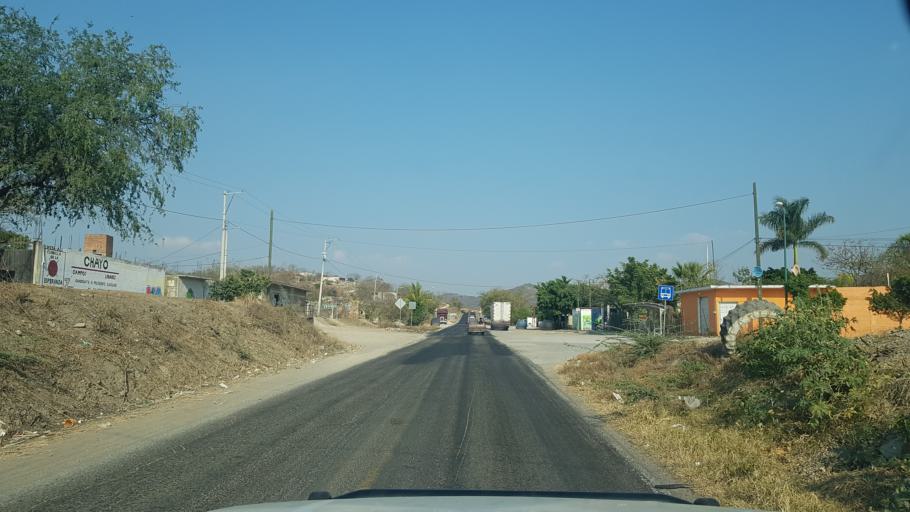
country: MX
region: Puebla
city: Calmeca
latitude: 18.6434
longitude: -98.6297
